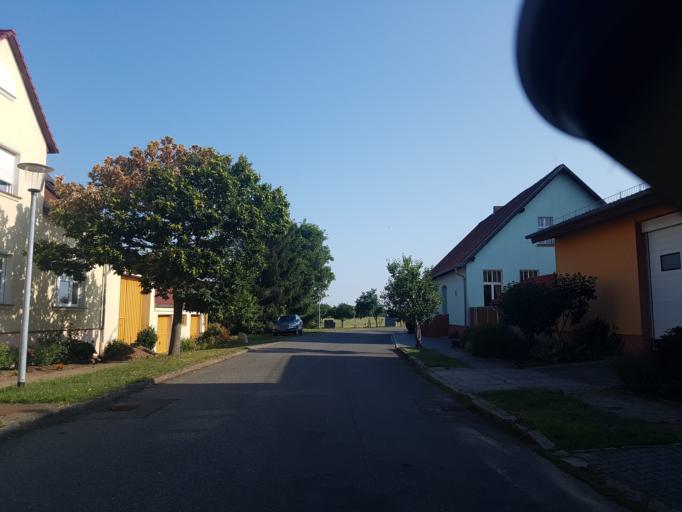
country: DE
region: Brandenburg
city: Niemegk
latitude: 52.1298
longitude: 12.7053
